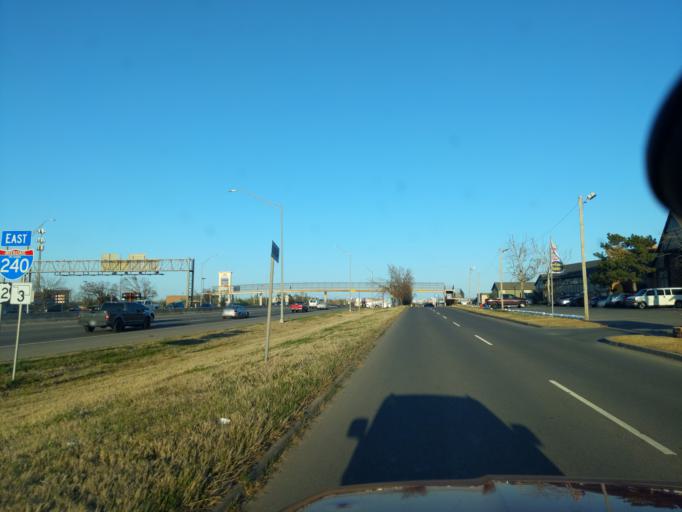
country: US
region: Oklahoma
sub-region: Cleveland County
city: Moore
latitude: 35.3911
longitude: -97.5416
